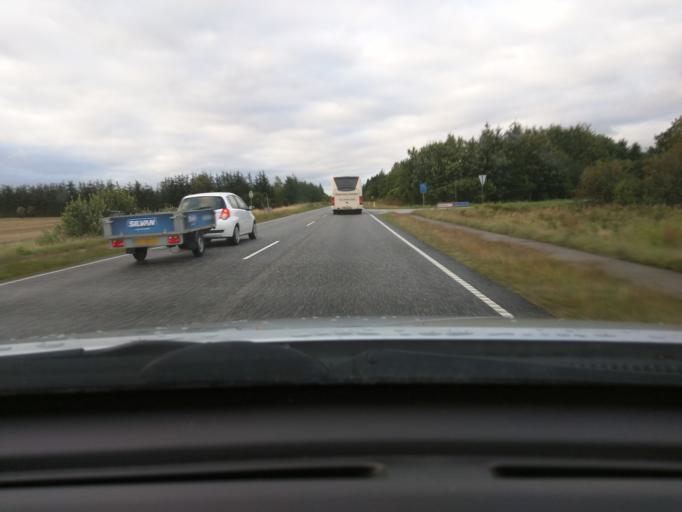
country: DK
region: Central Jutland
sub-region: Ikast-Brande Kommune
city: Bording Kirkeby
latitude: 56.2443
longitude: 9.3220
